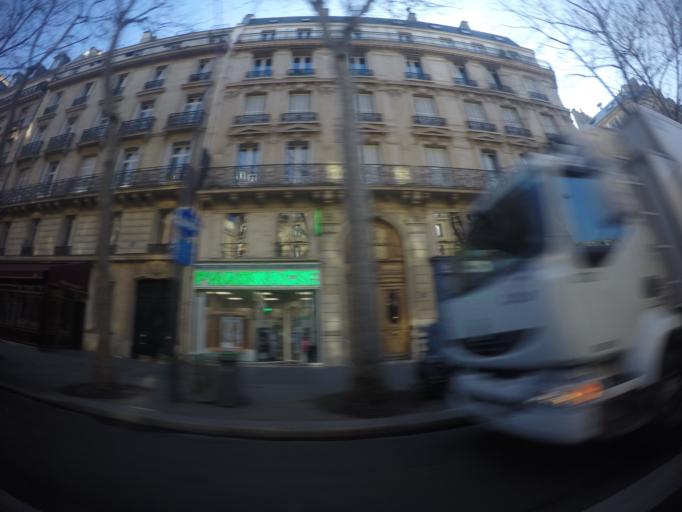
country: FR
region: Ile-de-France
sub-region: Paris
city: Paris
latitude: 48.8602
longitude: 2.3102
